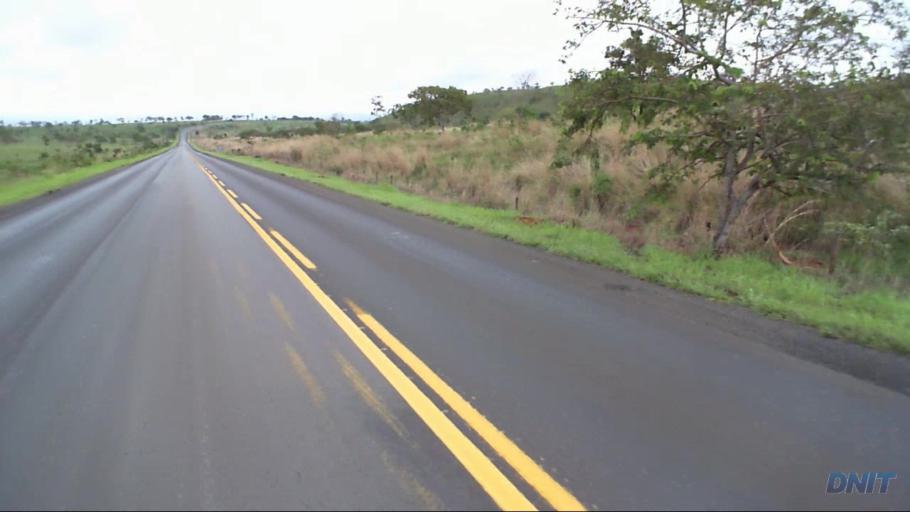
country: BR
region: Goias
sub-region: Padre Bernardo
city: Padre Bernardo
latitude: -15.2064
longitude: -48.4648
